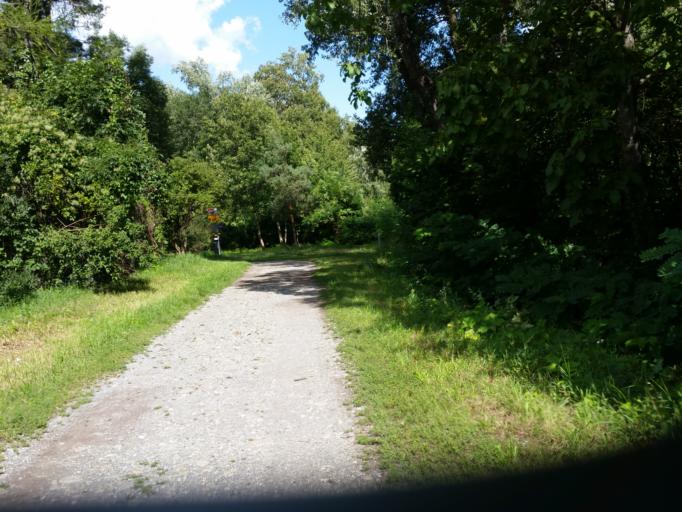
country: CH
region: Valais
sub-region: Sion District
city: Sitten
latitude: 46.2159
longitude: 7.3453
